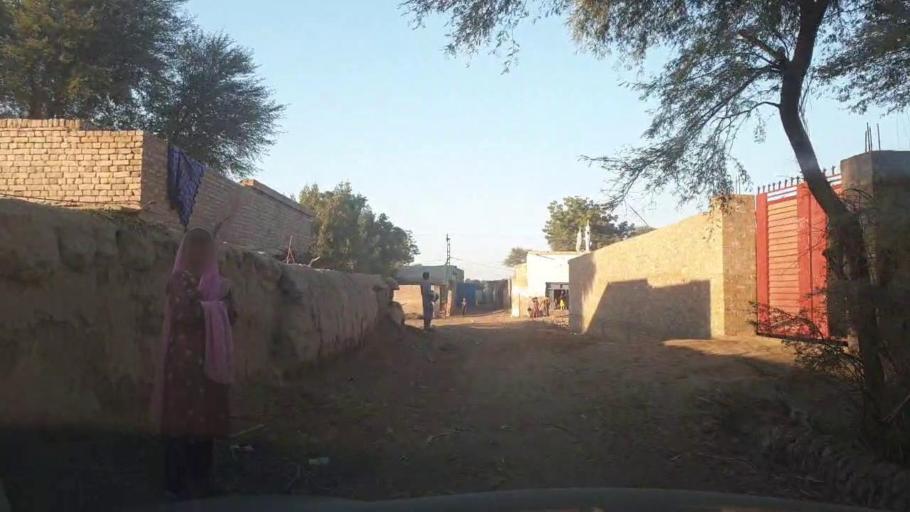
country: PK
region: Sindh
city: Ghotki
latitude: 28.0687
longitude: 69.3545
